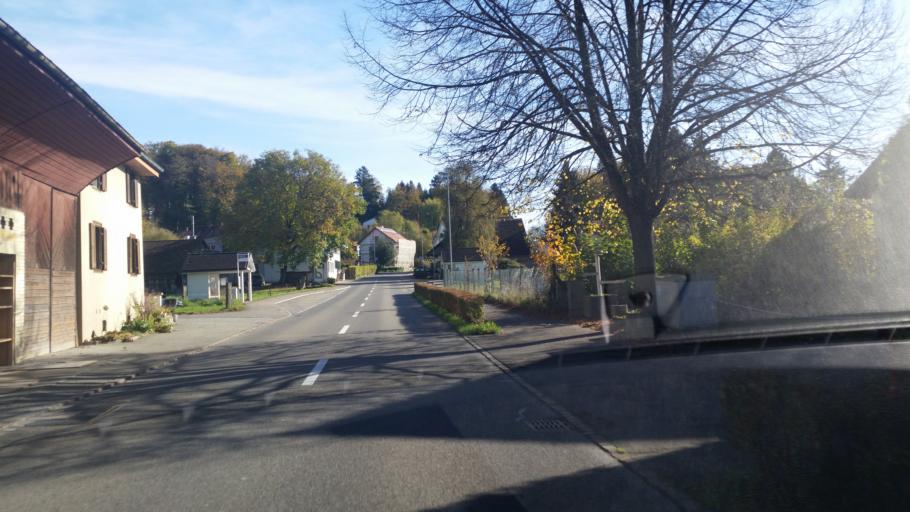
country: CH
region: Aargau
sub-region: Bezirk Baden
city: Niederrohrdorf
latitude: 47.4159
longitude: 8.3120
